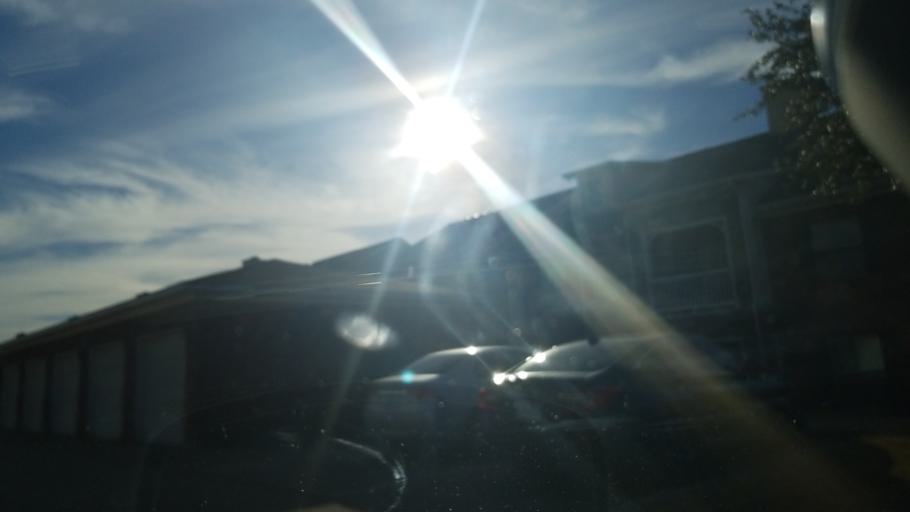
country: US
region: Texas
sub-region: Denton County
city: Corinth
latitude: 33.1428
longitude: -97.0571
